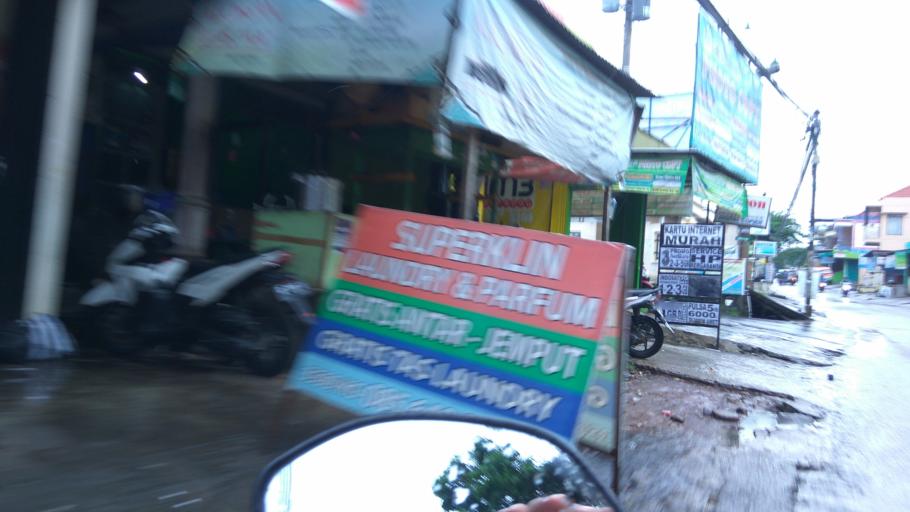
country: ID
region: Central Java
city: Semarang
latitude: -7.0523
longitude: 110.3949
